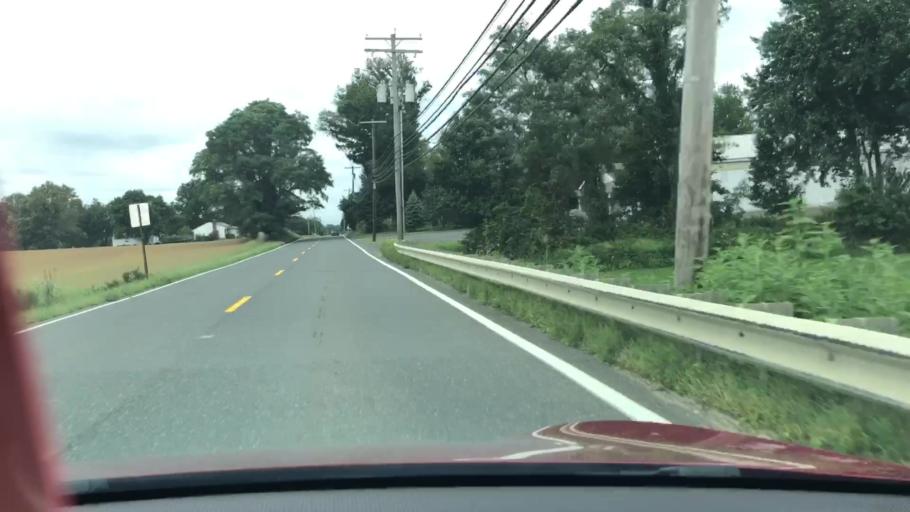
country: US
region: New Jersey
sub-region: Monmouth County
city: Allentown
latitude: 40.1742
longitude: -74.5597
